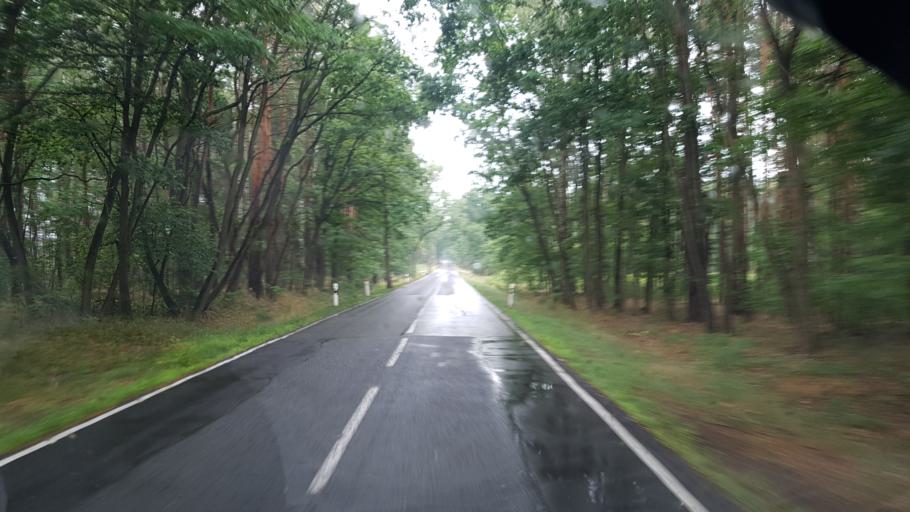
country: DE
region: Brandenburg
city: Lebusa
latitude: 51.8200
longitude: 13.4187
